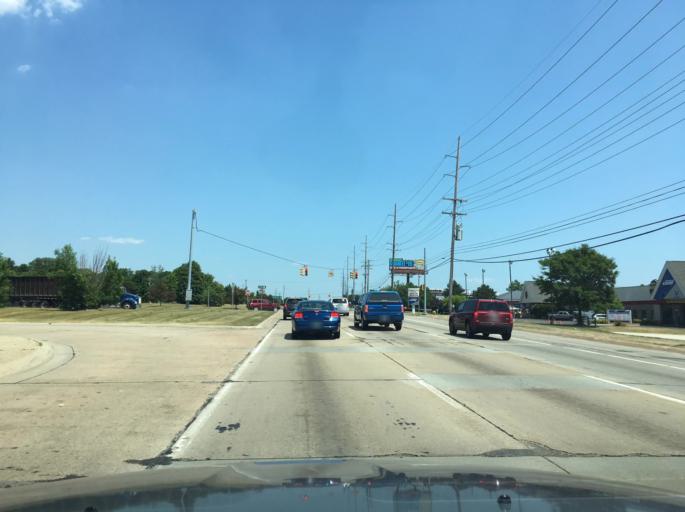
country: US
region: Michigan
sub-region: Macomb County
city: Mount Clemens
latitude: 42.6293
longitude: -82.8794
